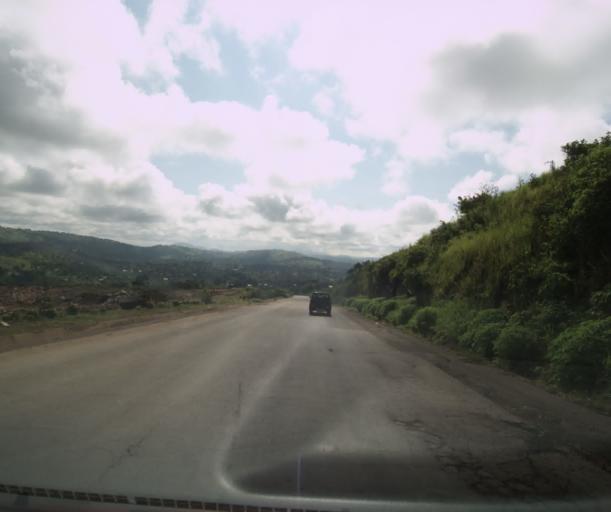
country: CM
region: West
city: Bafoussam
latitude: 5.4826
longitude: 10.4956
